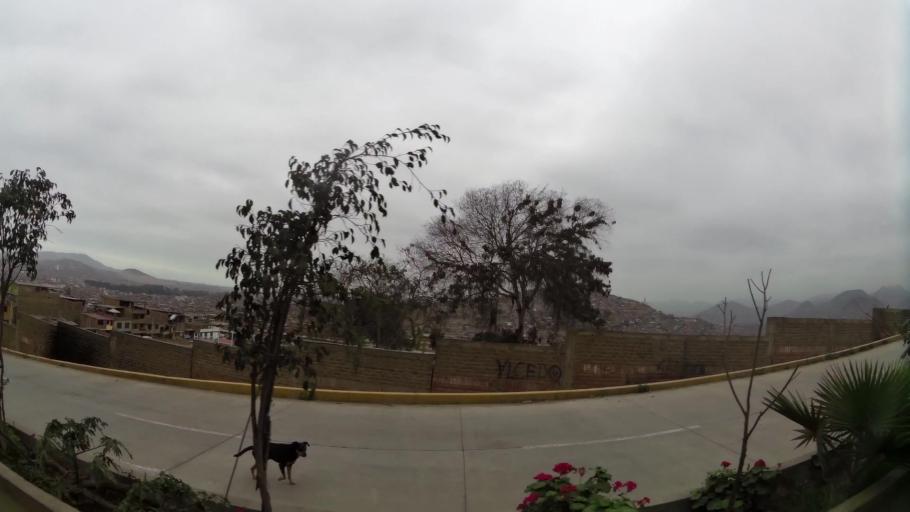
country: PE
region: Lima
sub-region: Lima
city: Surco
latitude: -12.1966
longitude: -76.9491
